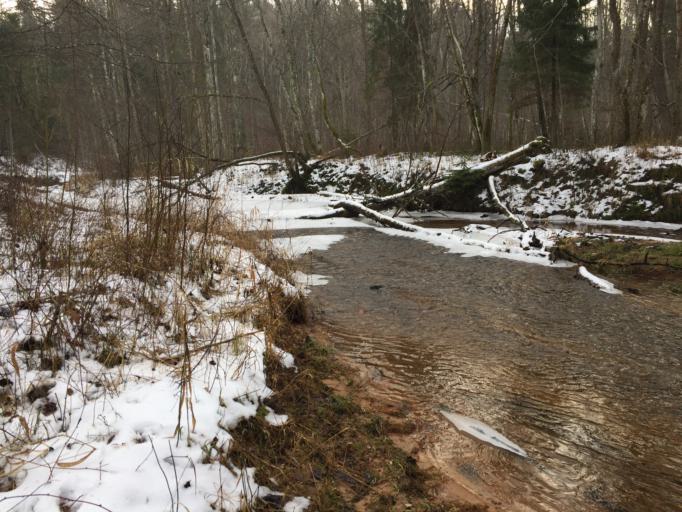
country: LV
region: Priekuli
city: Priekuli
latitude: 57.3339
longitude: 25.3995
